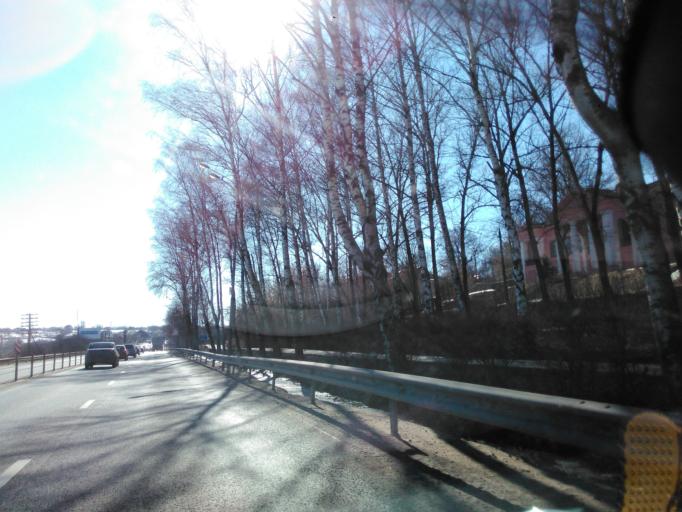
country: RU
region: Moskovskaya
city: Iksha
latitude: 56.1671
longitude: 37.5039
